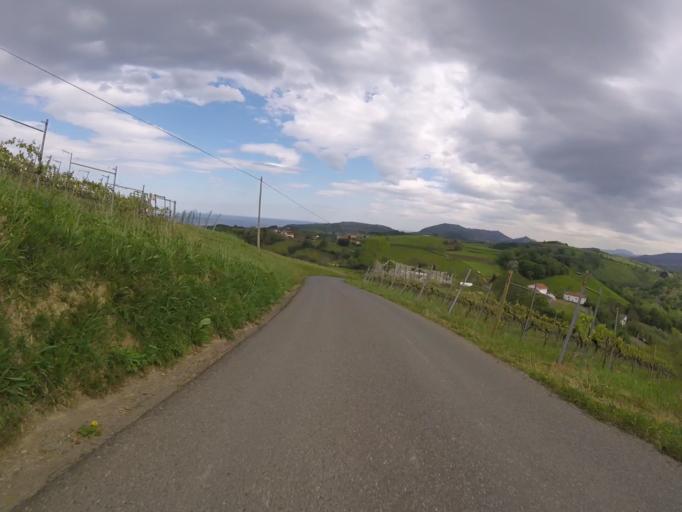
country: ES
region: Basque Country
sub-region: Provincia de Guipuzcoa
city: Zarautz
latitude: 43.2588
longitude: -2.1715
